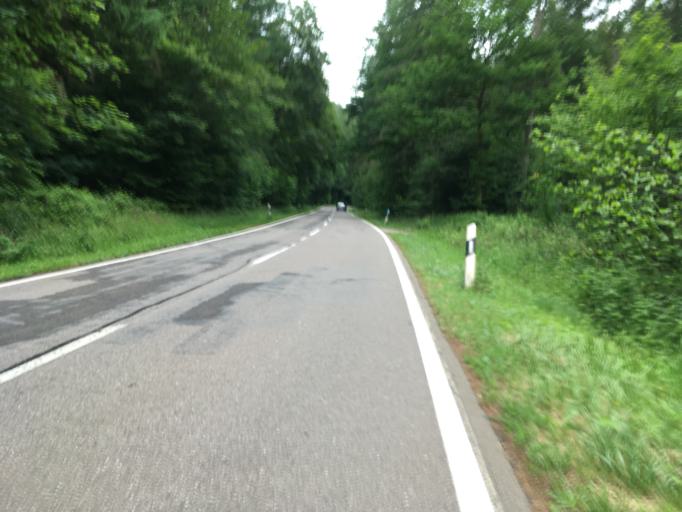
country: DE
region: Saarland
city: Saarhoelzbach
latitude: 49.4940
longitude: 6.6308
